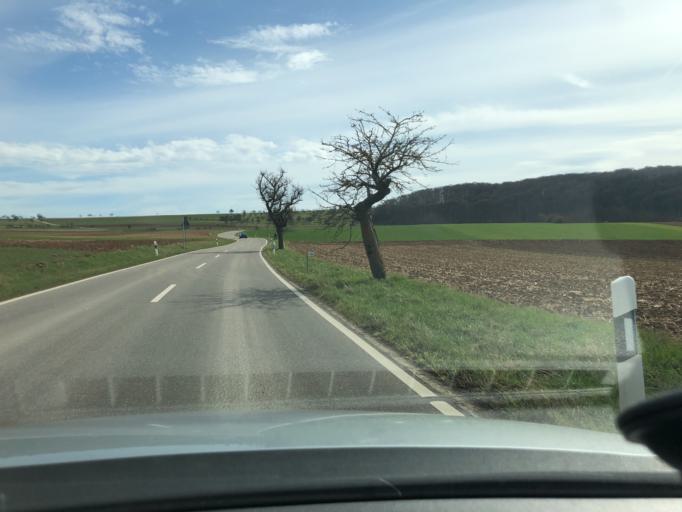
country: DE
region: Baden-Wuerttemberg
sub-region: Karlsruhe Region
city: Illingen
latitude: 48.9311
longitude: 8.9222
